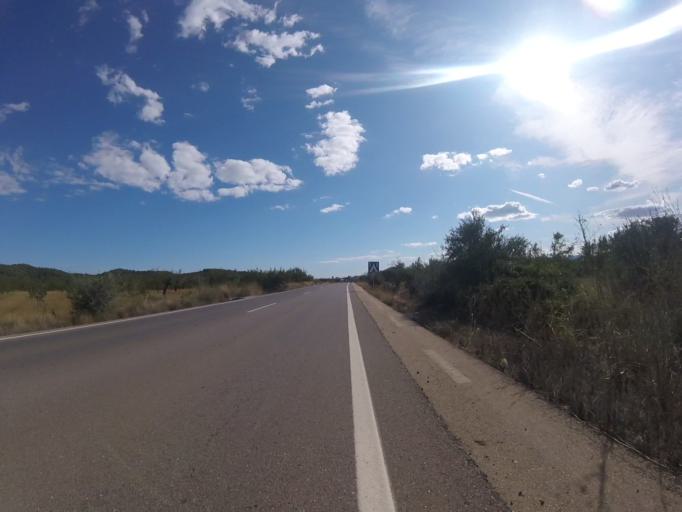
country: ES
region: Valencia
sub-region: Provincia de Castello
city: Alcala de Xivert
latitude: 40.2605
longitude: 0.2437
